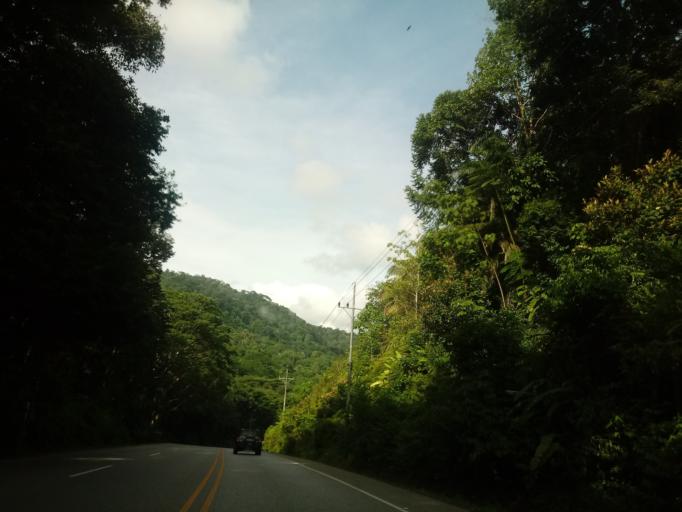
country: CR
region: San Jose
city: Daniel Flores
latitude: 9.1999
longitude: -83.7875
